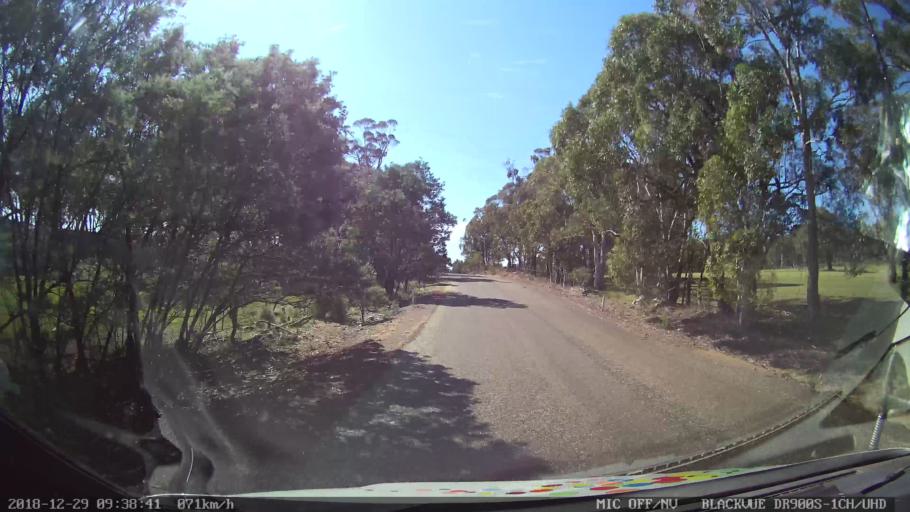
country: AU
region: New South Wales
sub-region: Upper Lachlan Shire
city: Crookwell
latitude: -34.6491
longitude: 149.3776
